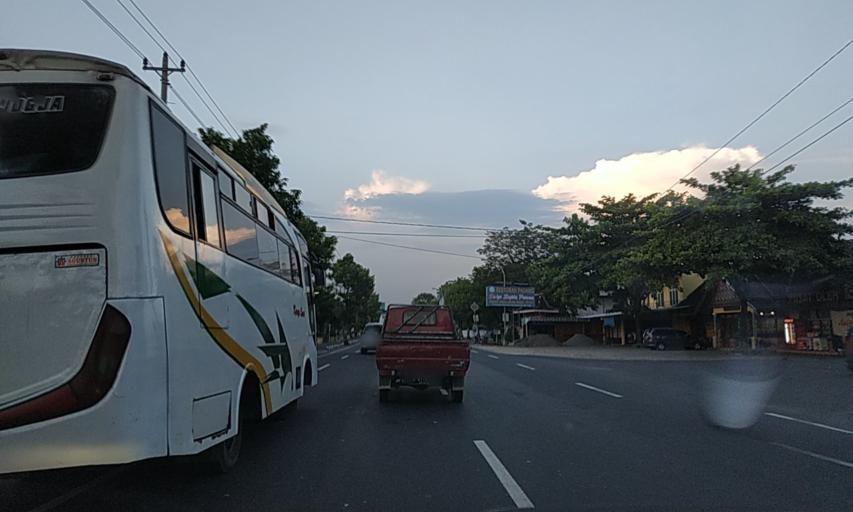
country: ID
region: Daerah Istimewa Yogyakarta
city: Srandakan
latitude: -7.8669
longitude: 110.1497
